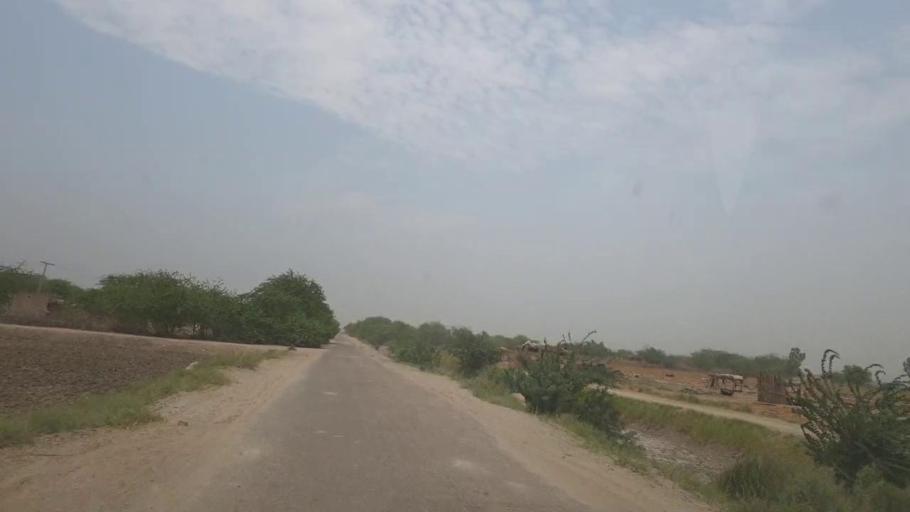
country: PK
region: Sindh
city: Kot Diji
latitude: 27.4374
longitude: 68.7125
